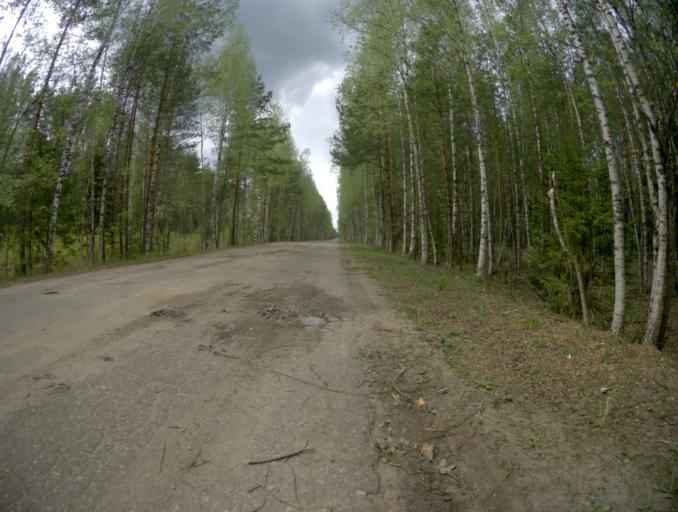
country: RU
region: Vladimir
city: Velikodvorskiy
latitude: 55.2434
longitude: 40.7336
